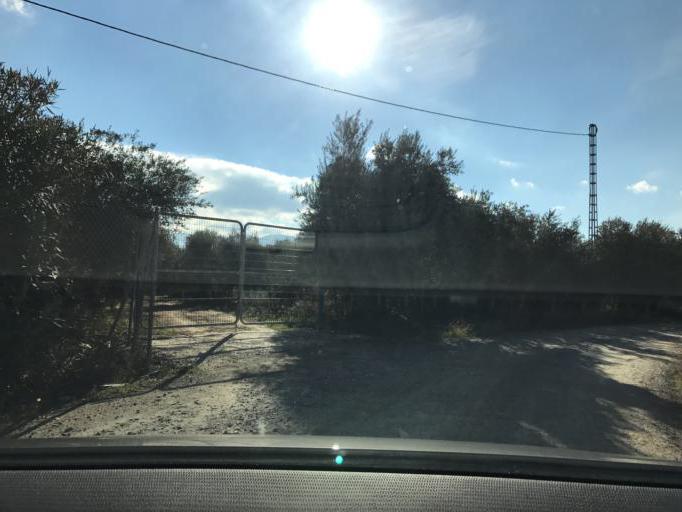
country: ES
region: Andalusia
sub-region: Provincia de Granada
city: Gojar
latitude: 37.1031
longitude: -3.6218
